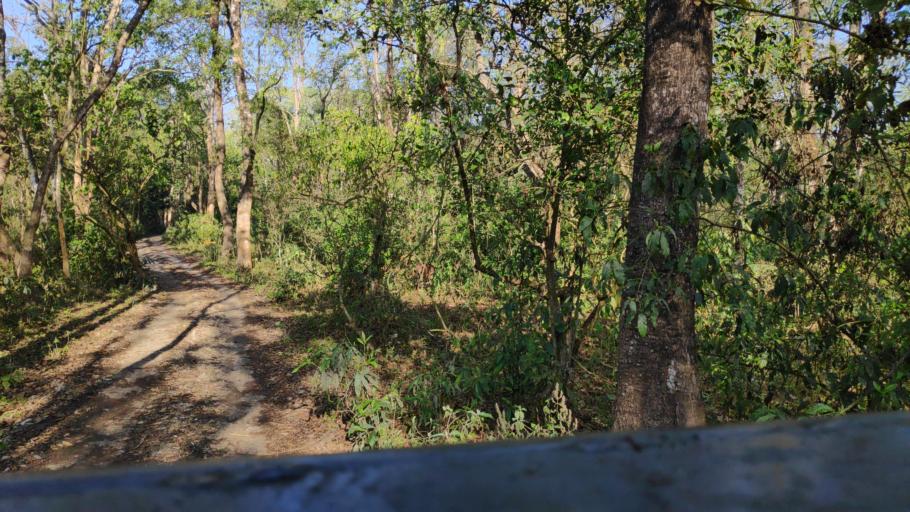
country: NP
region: Central Region
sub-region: Narayani Zone
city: Bharatpur
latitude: 27.5599
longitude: 84.5403
